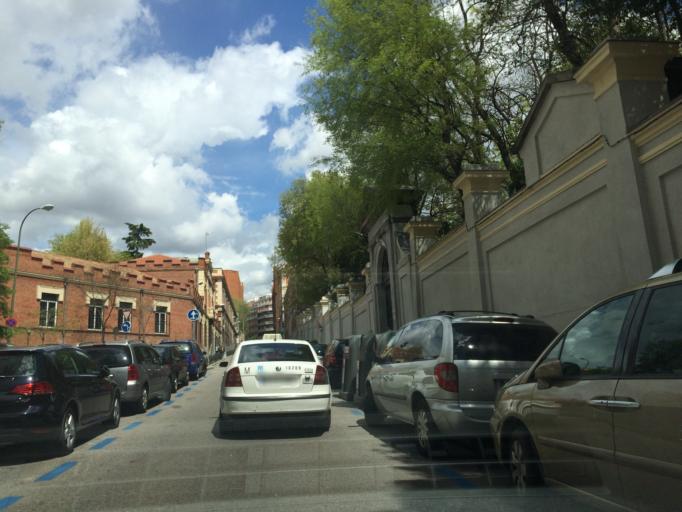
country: ES
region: Madrid
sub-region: Provincia de Madrid
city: Chamberi
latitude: 40.4281
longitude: -3.7135
